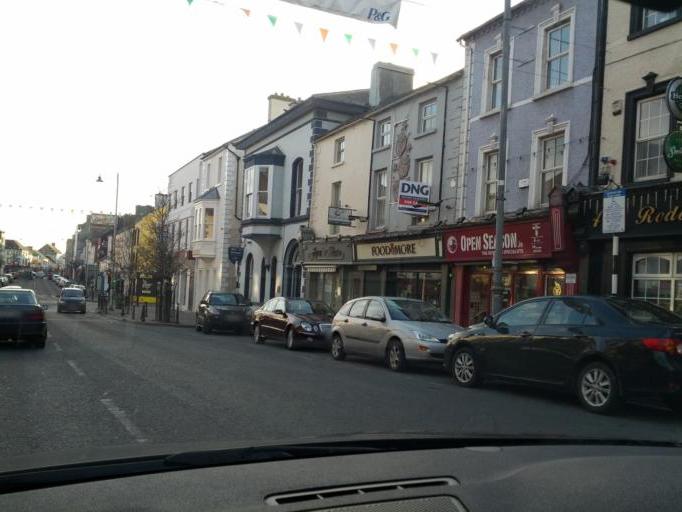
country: IE
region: Munster
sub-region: North Tipperary
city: Nenagh
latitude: 52.8644
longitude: -8.1975
